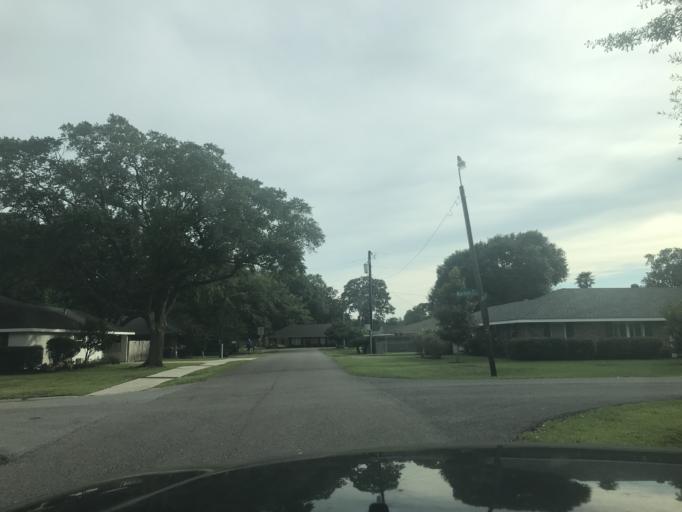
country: US
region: Louisiana
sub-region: Lafayette Parish
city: Lafayette
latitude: 30.1927
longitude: -92.0480
